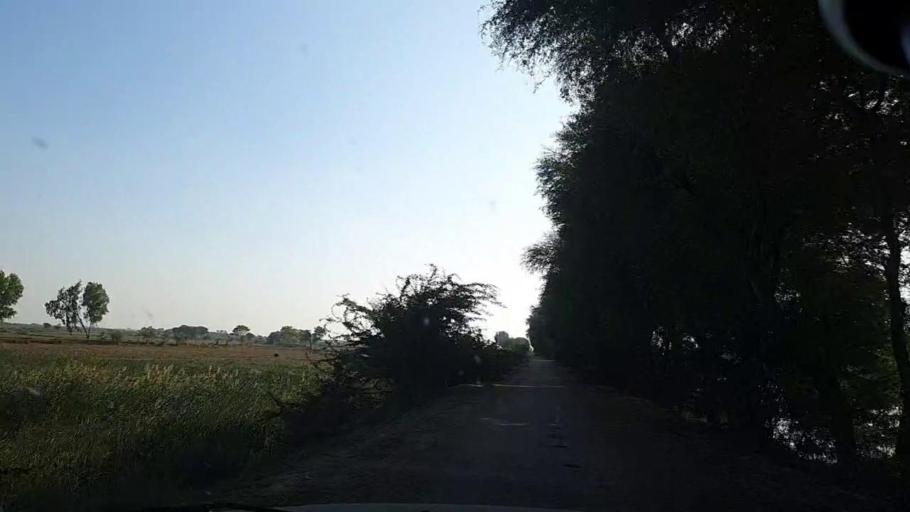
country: PK
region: Sindh
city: Chuhar Jamali
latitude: 24.5662
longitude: 68.0415
